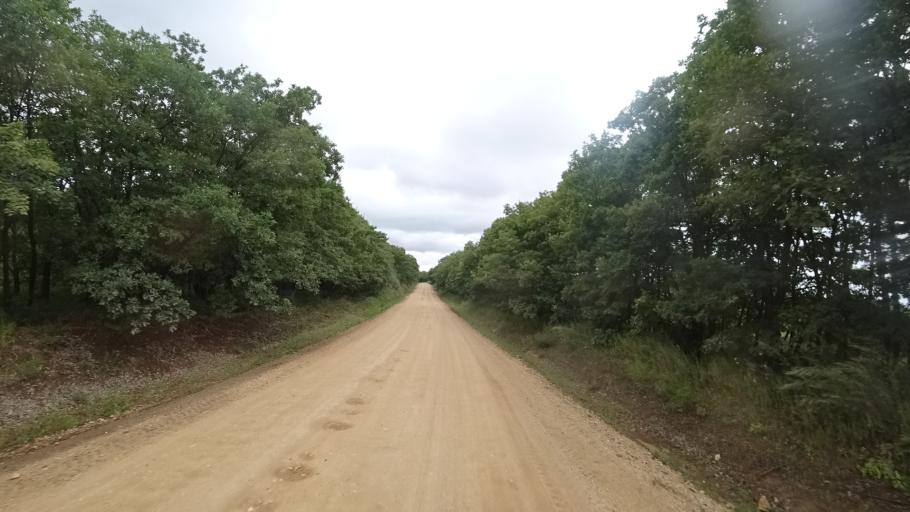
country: RU
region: Primorskiy
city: Chernigovka
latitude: 44.3418
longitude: 132.6202
